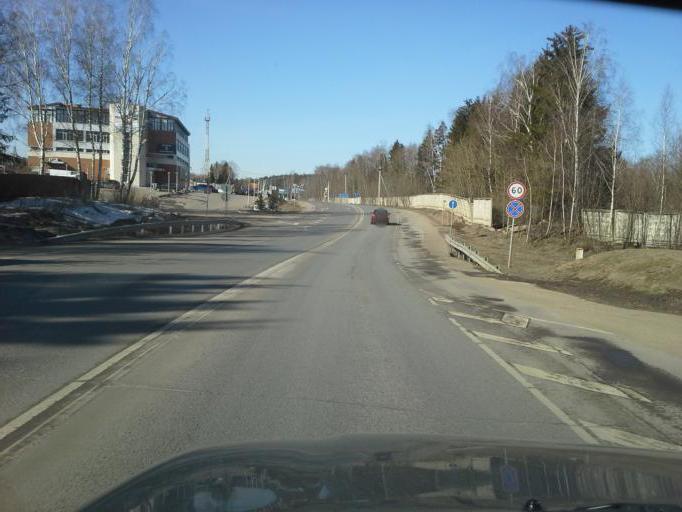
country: RU
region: Moskovskaya
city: Gorki Vtoryye
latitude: 55.6818
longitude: 37.1464
